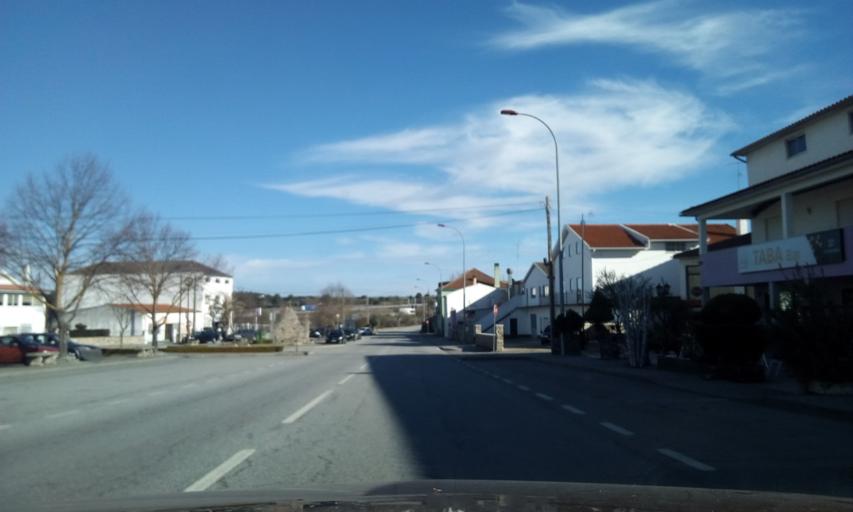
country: ES
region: Castille and Leon
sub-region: Provincia de Salamanca
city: Fuentes de Onoro
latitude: 40.6148
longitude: -6.8371
